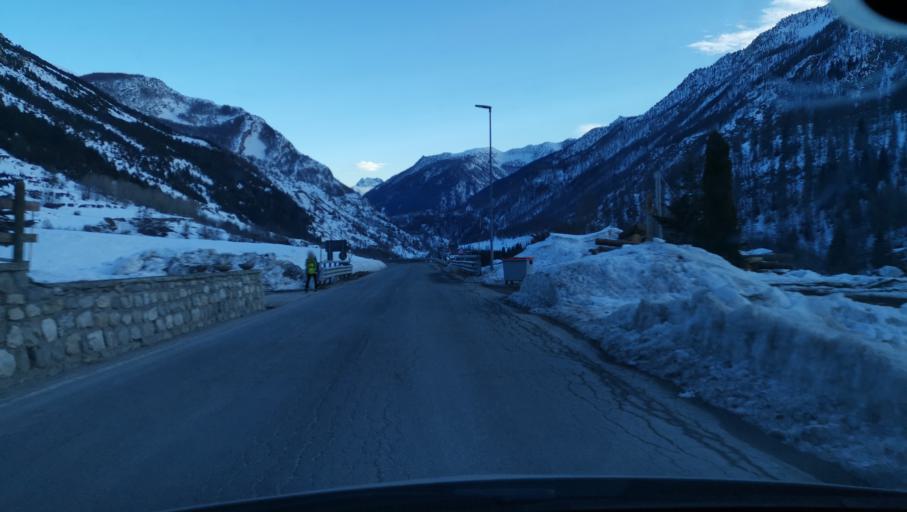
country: IT
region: Piedmont
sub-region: Provincia di Cuneo
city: Bersezio
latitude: 44.3750
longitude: 6.9745
